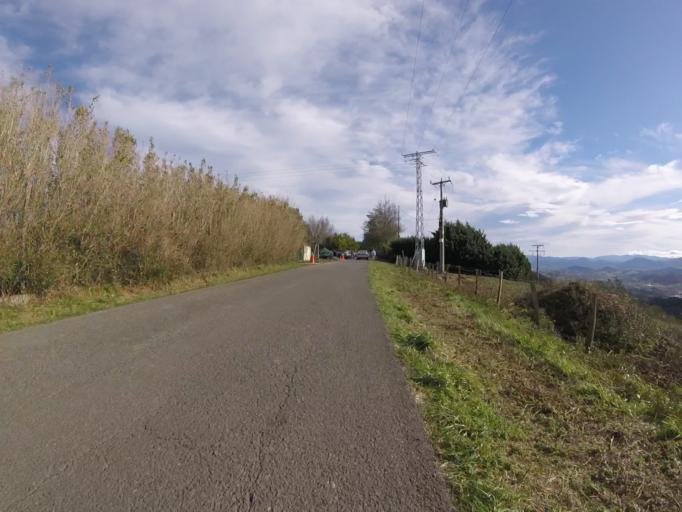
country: ES
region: Basque Country
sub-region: Provincia de Guipuzcoa
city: Orio
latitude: 43.2935
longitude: -2.0910
